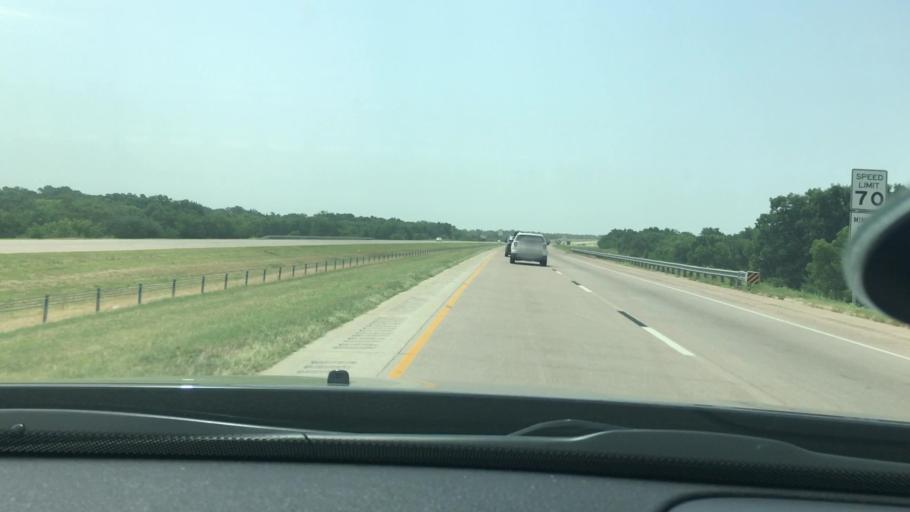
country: US
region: Oklahoma
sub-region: Garvin County
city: Pauls Valley
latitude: 34.6976
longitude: -97.2378
